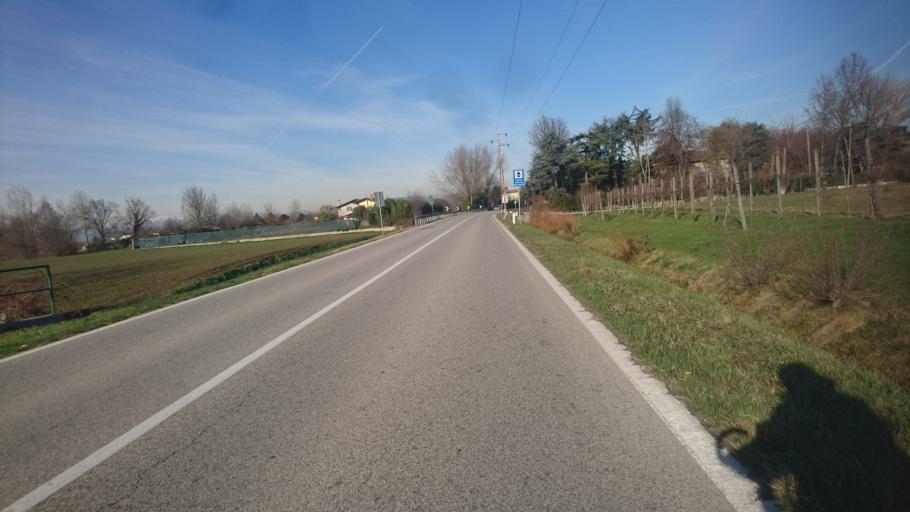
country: IT
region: Veneto
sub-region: Provincia di Padova
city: Villafranca Padovana
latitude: 45.5101
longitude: 11.7878
